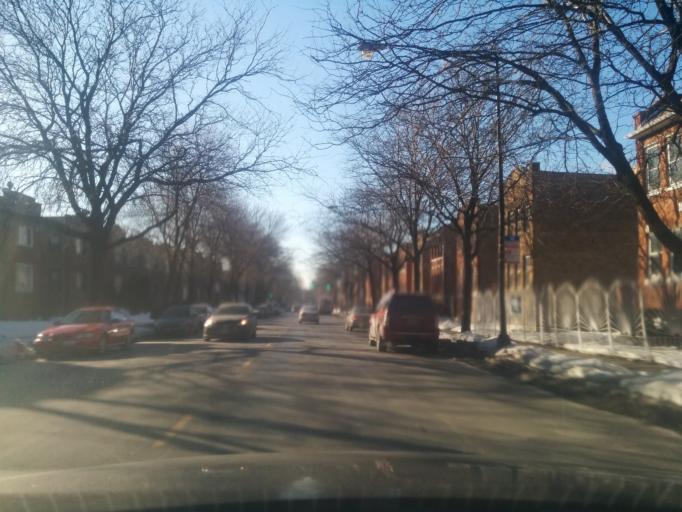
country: US
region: Illinois
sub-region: Cook County
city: Oak Park
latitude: 41.9123
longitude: -87.7754
